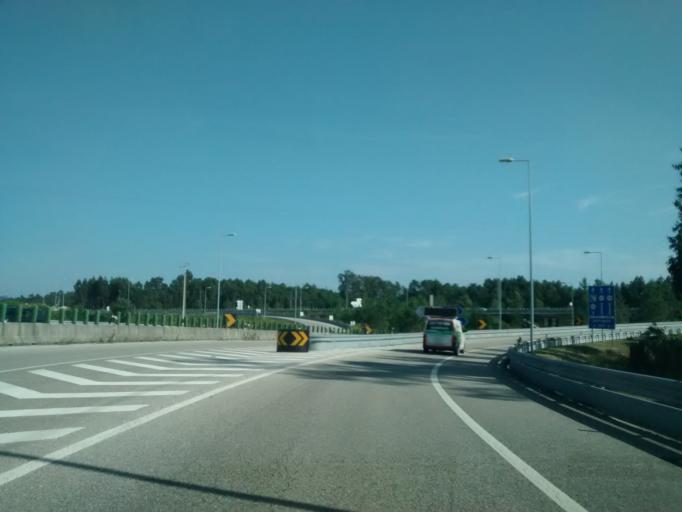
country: PT
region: Leiria
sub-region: Pombal
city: Lourical
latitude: 39.9900
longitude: -8.7885
